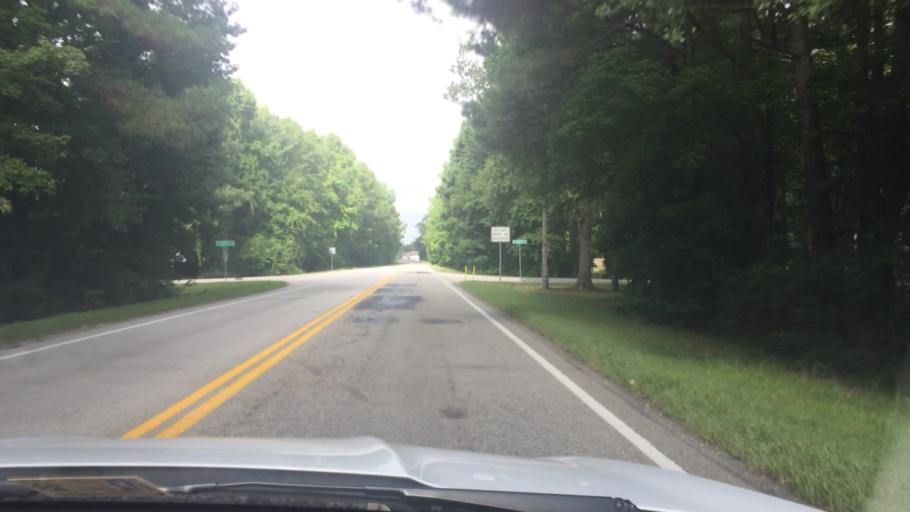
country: US
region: Virginia
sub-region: City of Poquoson
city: Poquoson
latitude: 37.1216
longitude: -76.4393
